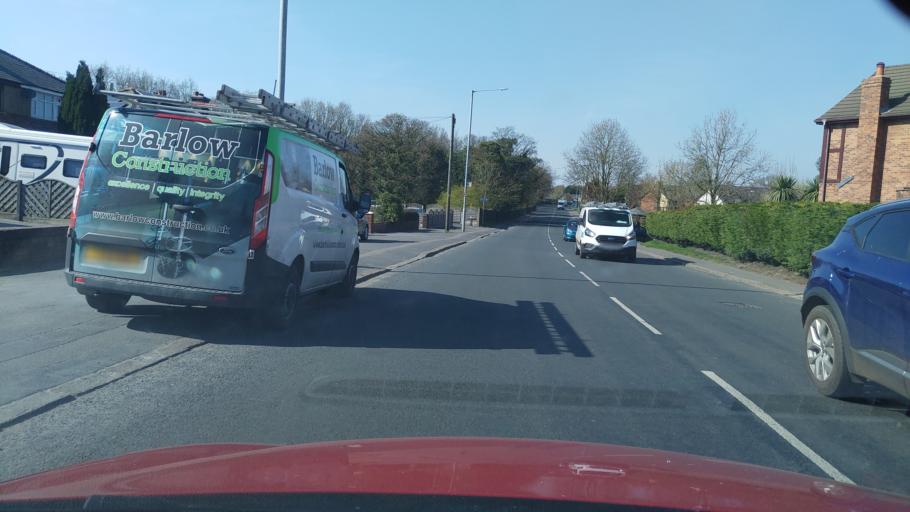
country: GB
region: England
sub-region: Lancashire
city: Adlington
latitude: 53.6191
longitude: -2.6106
